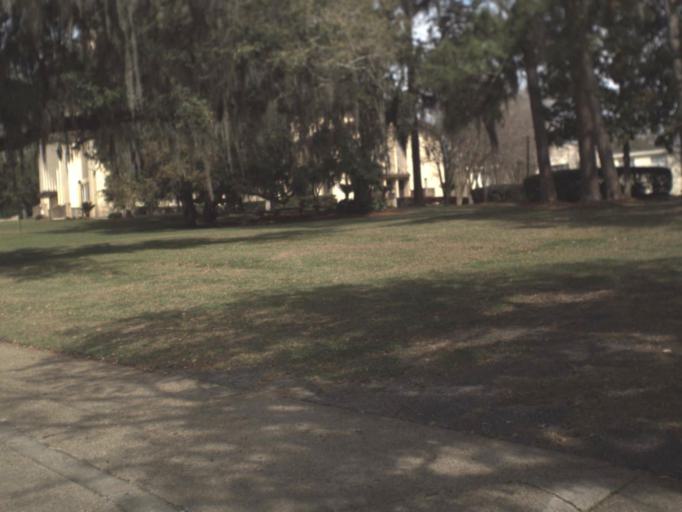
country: US
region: Florida
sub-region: Leon County
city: Tallahassee
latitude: 30.4458
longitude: -84.2972
